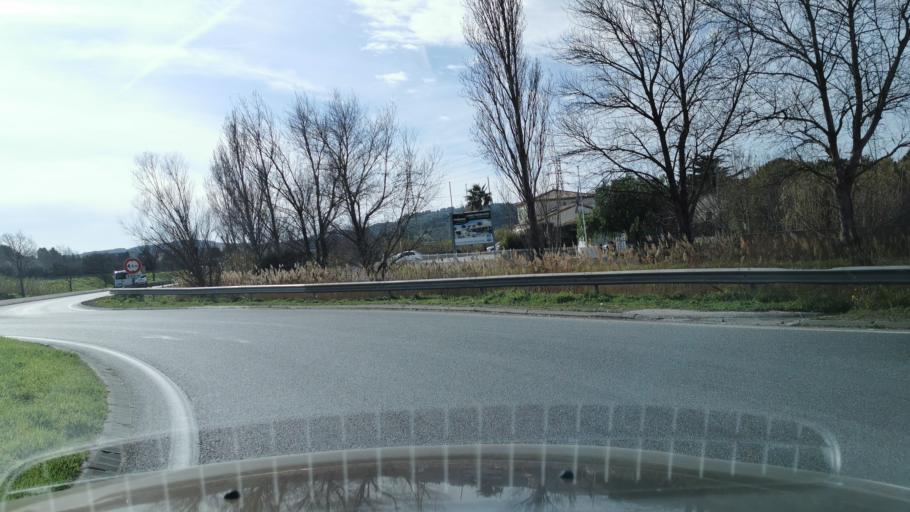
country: FR
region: Languedoc-Roussillon
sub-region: Departement de l'Aude
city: Narbonne
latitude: 43.1934
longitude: 2.9804
